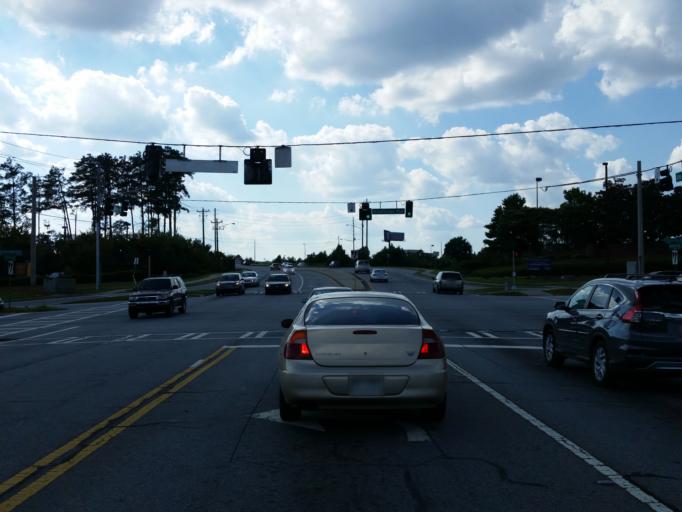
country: US
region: Georgia
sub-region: Gwinnett County
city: Duluth
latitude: 33.9579
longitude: -84.1103
